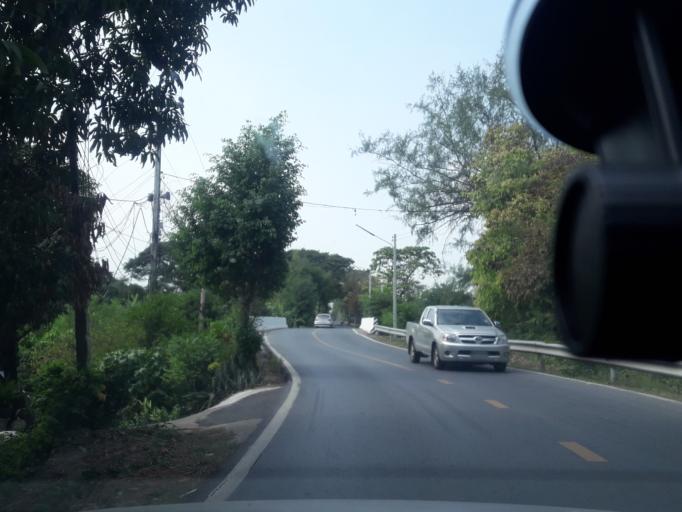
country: TH
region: Sara Buri
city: Nong Khae
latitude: 14.3351
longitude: 100.8692
